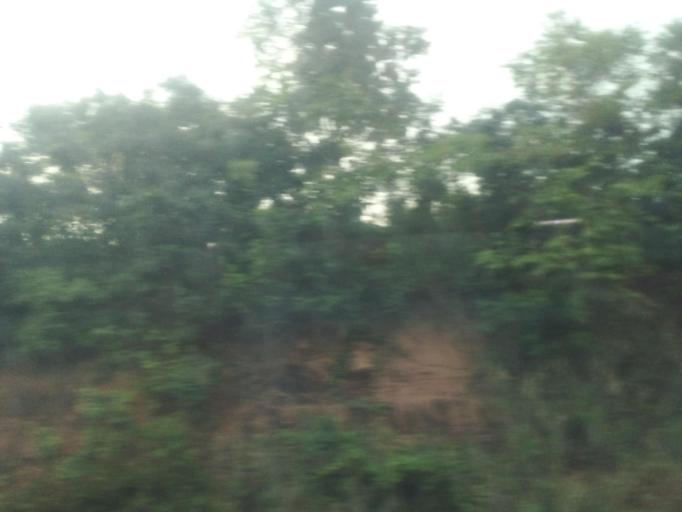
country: BR
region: Maranhao
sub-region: Imperatriz
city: Imperatriz
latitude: -4.9208
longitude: -47.4221
